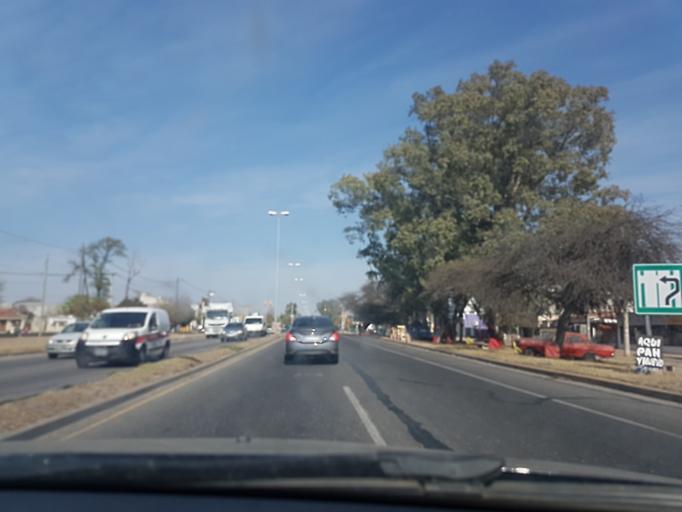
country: AR
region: Cordoba
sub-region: Departamento de Capital
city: Cordoba
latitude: -31.4721
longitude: -64.2304
